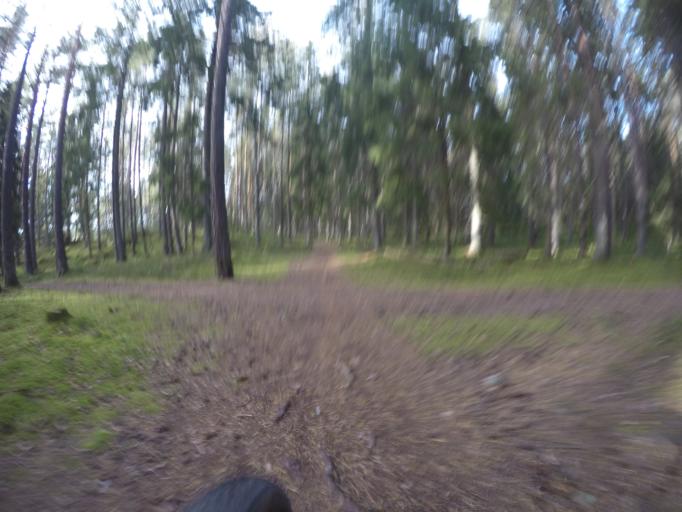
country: SE
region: Vaestmanland
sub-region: Kopings Kommun
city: Koping
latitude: 59.5339
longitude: 15.9965
